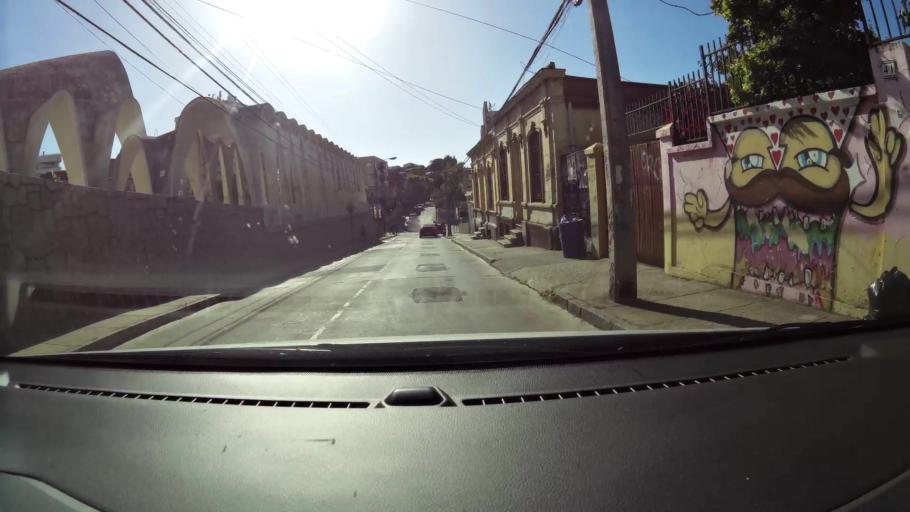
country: CL
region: Valparaiso
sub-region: Provincia de Valparaiso
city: Vina del Mar
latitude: -33.0283
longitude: -71.5623
